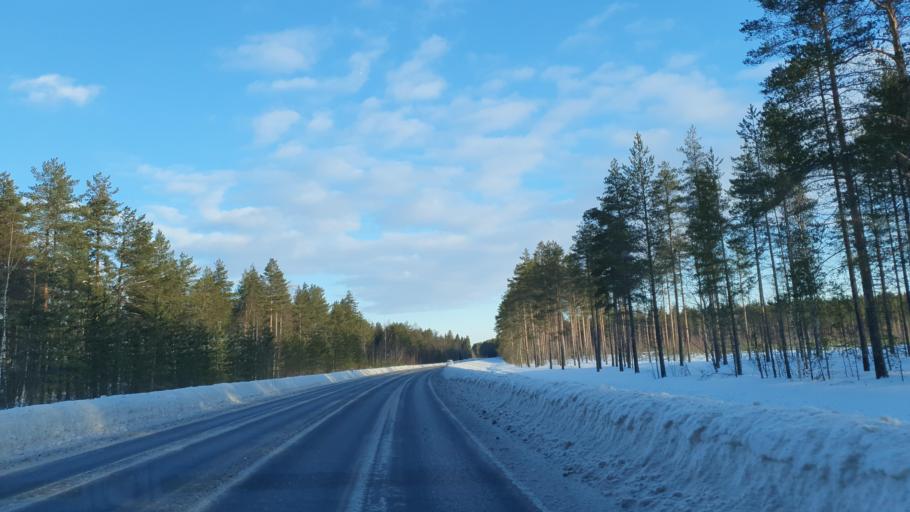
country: FI
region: Northern Ostrobothnia
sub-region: Oulunkaari
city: Utajaervi
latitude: 64.6804
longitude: 26.5355
